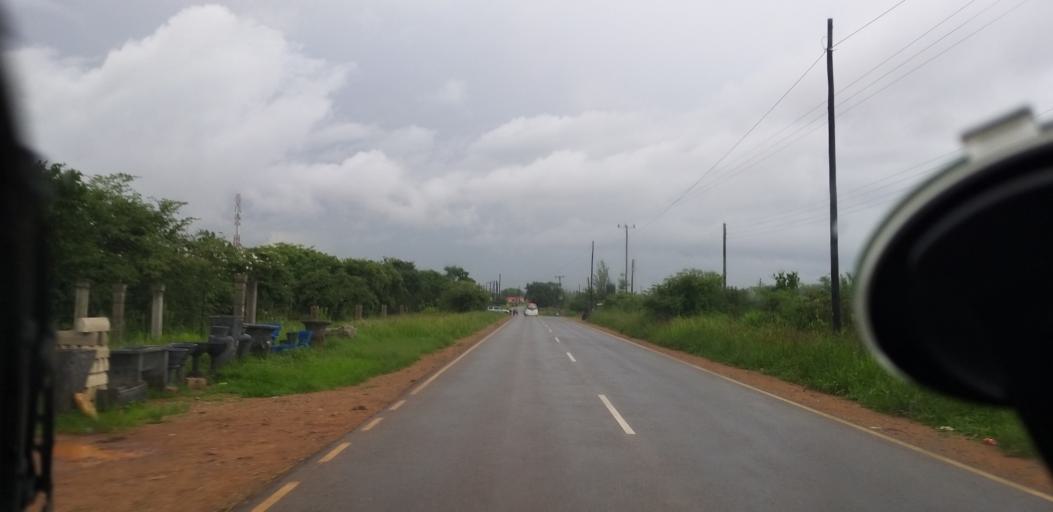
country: ZM
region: Lusaka
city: Lusaka
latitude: -15.4923
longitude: 28.3136
